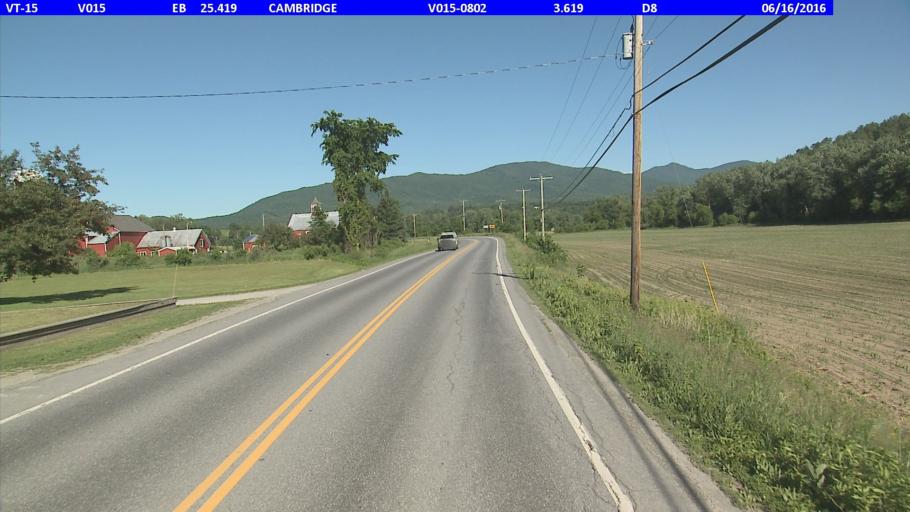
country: US
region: Vermont
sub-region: Lamoille County
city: Johnson
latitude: 44.6454
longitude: -72.8570
